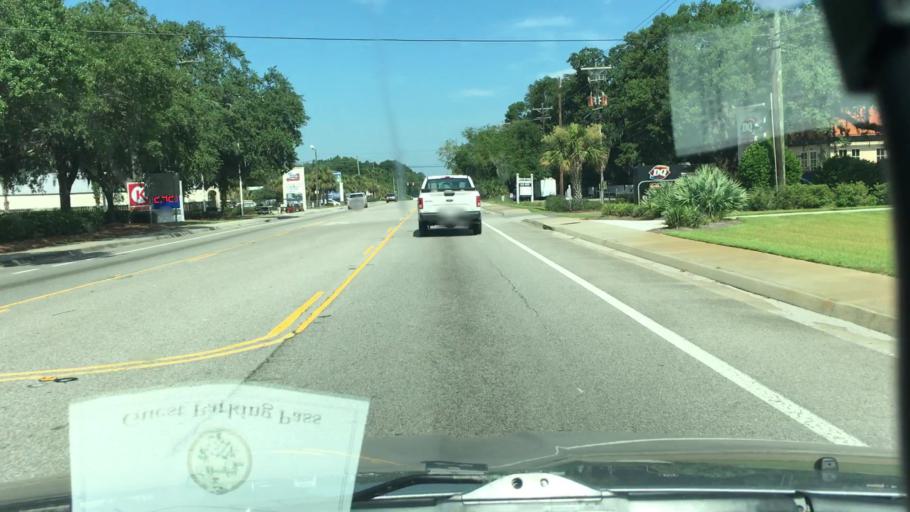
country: US
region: South Carolina
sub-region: Beaufort County
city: Beaufort
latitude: 32.4160
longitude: -80.6546
